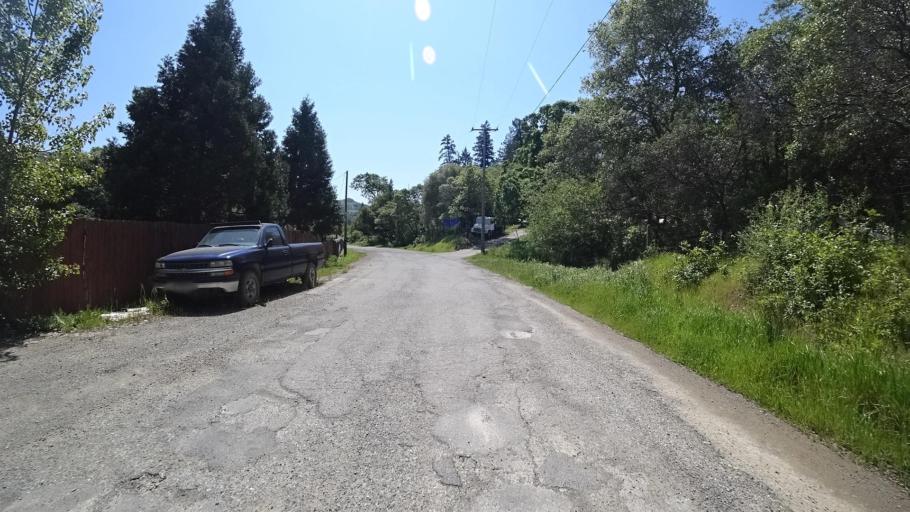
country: US
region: California
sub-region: Humboldt County
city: Redway
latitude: 40.1686
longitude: -123.6048
